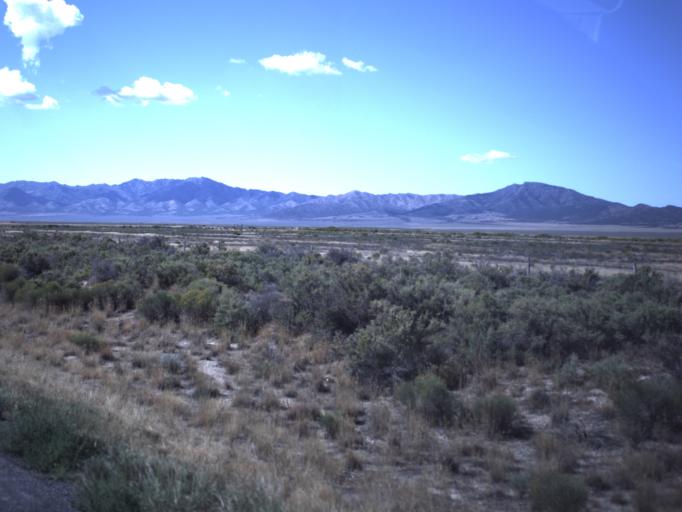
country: US
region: Utah
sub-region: Tooele County
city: Tooele
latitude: 40.1494
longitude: -112.4308
